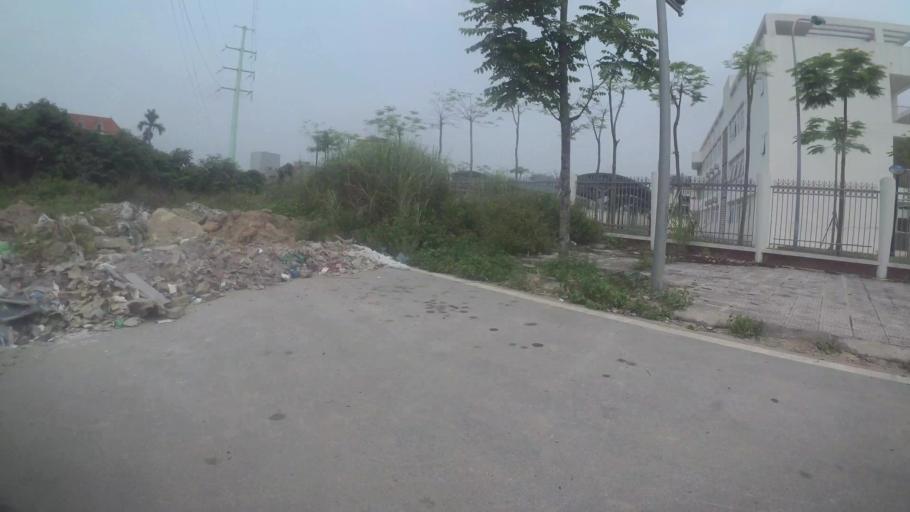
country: VN
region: Ha Noi
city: Cau Dien
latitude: 21.0325
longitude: 105.7472
